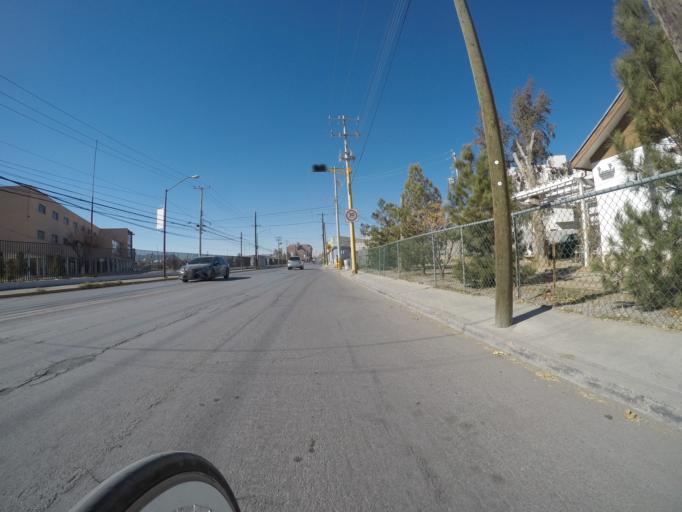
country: MX
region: Chihuahua
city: Ciudad Juarez
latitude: 31.7121
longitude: -106.4127
